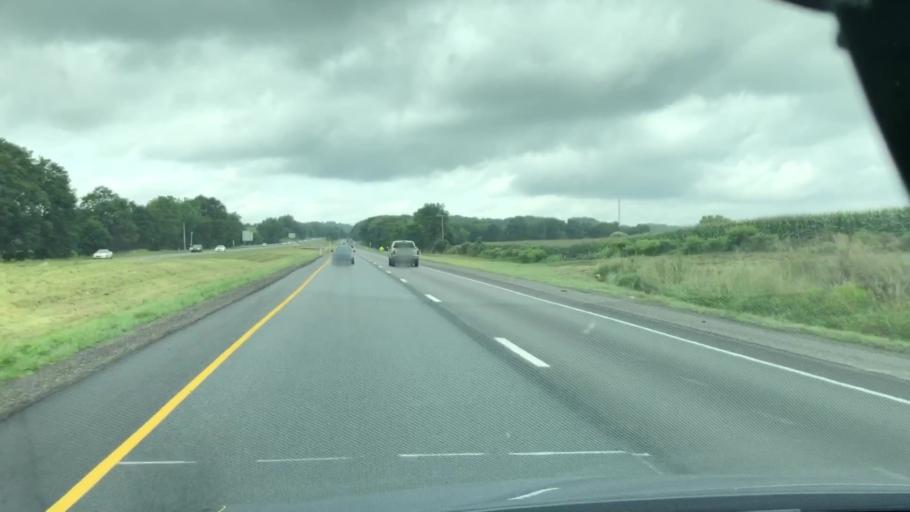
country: US
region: Pennsylvania
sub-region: Butler County
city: Prospect
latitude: 40.9735
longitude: -80.1327
